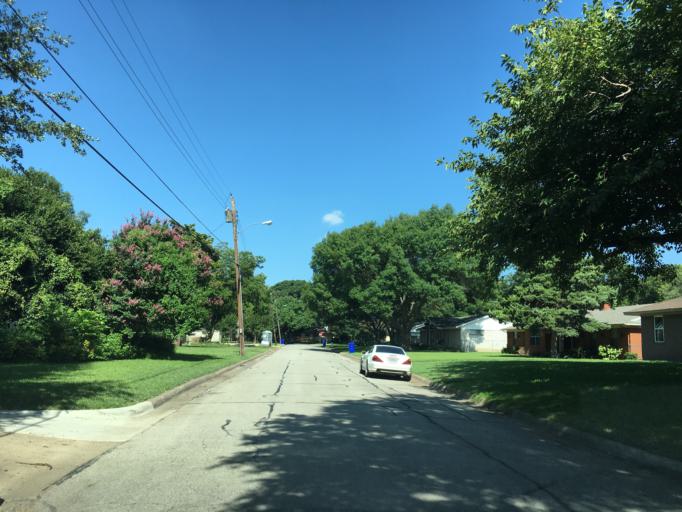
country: US
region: Texas
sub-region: Dallas County
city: Farmers Branch
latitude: 32.9190
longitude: -96.8750
